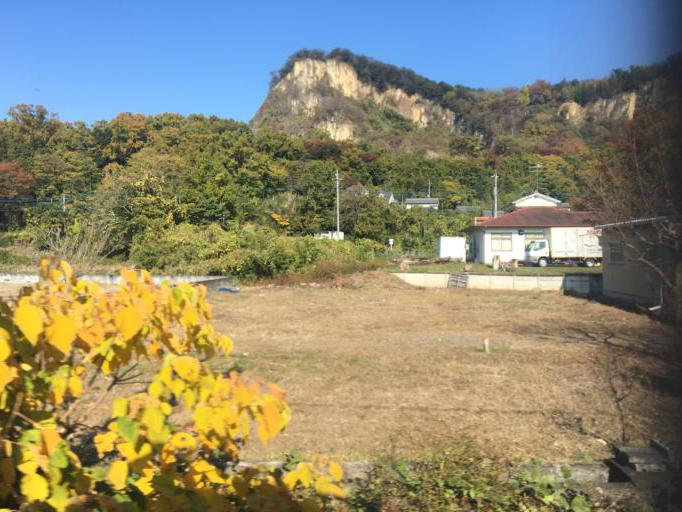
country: JP
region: Tochigi
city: Sano
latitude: 36.3267
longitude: 139.6544
